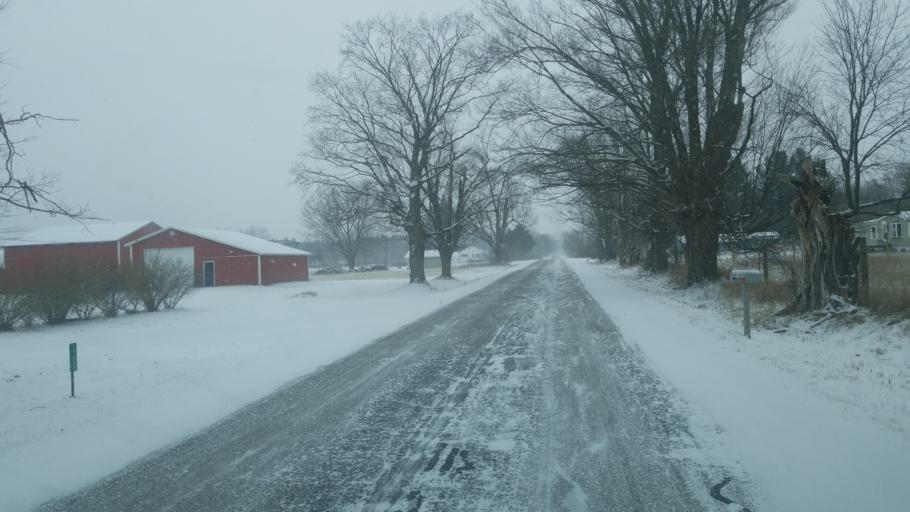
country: US
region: Michigan
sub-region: Mecosta County
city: Big Rapids
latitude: 43.7503
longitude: -85.4032
